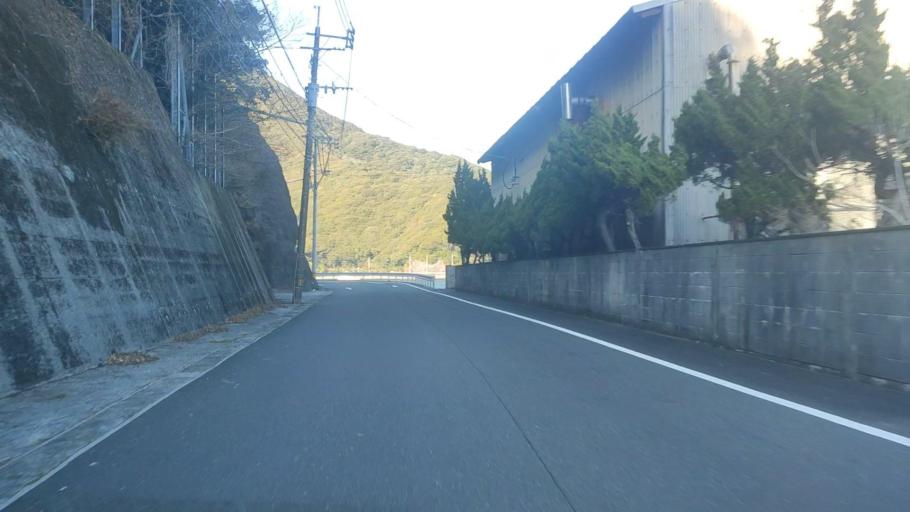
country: JP
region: Oita
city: Saiki
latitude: 32.8362
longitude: 131.9581
